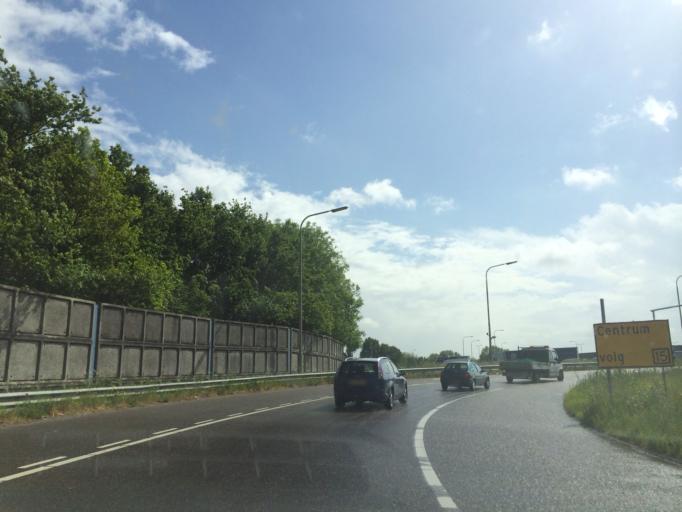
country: NL
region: South Holland
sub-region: Gemeente Capelle aan den IJssel
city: Capelle-West
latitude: 51.8988
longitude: 4.5501
